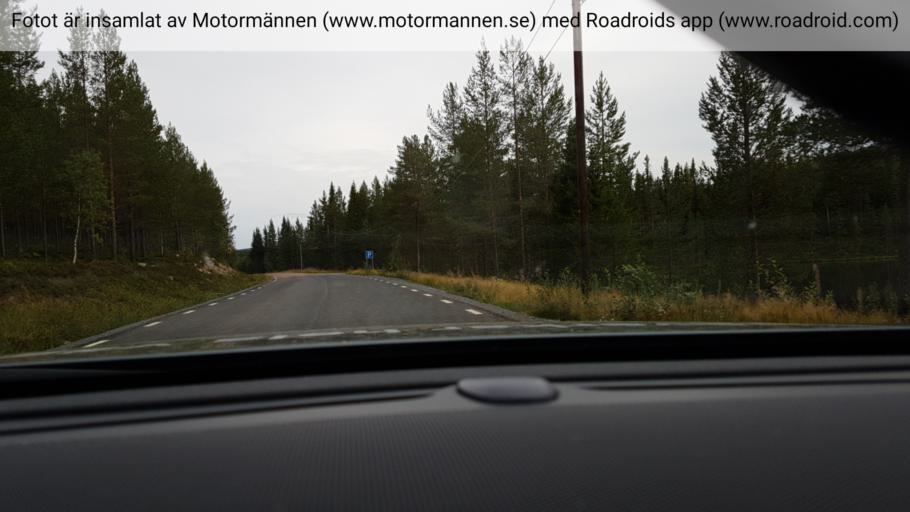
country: NO
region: Hedmark
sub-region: Trysil
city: Innbygda
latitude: 61.6657
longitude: 12.6987
